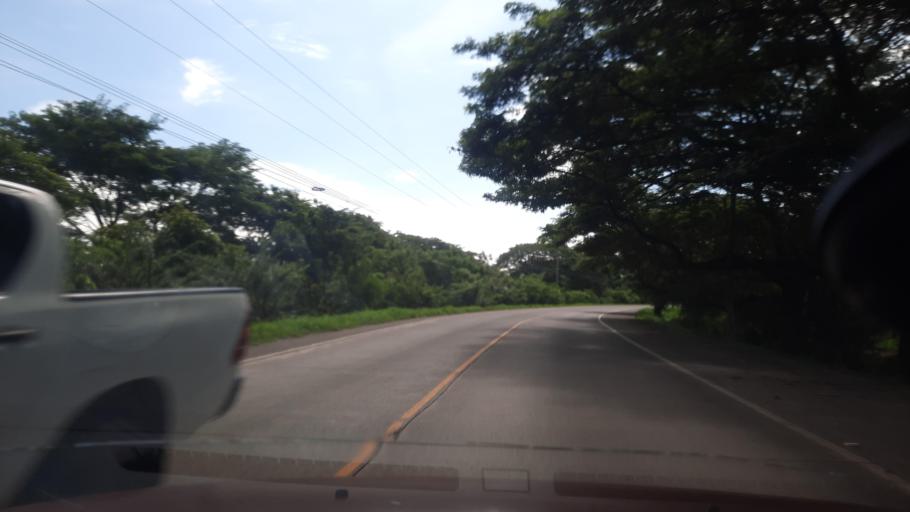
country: SV
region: La Paz
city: Zacatecoluca
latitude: 13.4458
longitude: -88.7459
